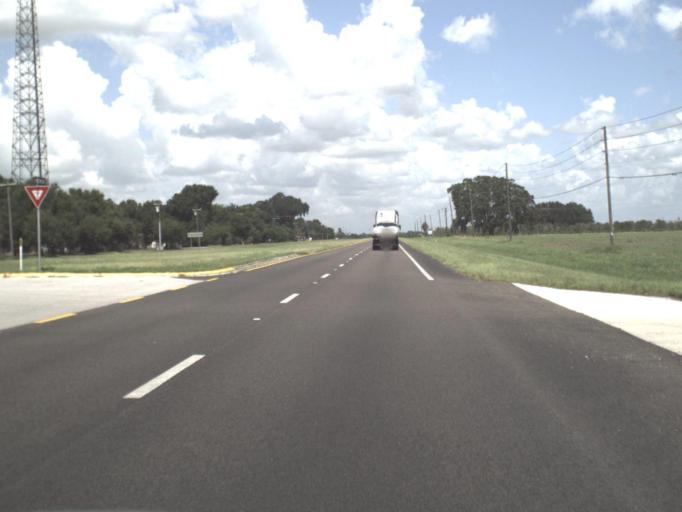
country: US
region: Florida
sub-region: Hardee County
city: Bowling Green
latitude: 27.6057
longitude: -81.8246
